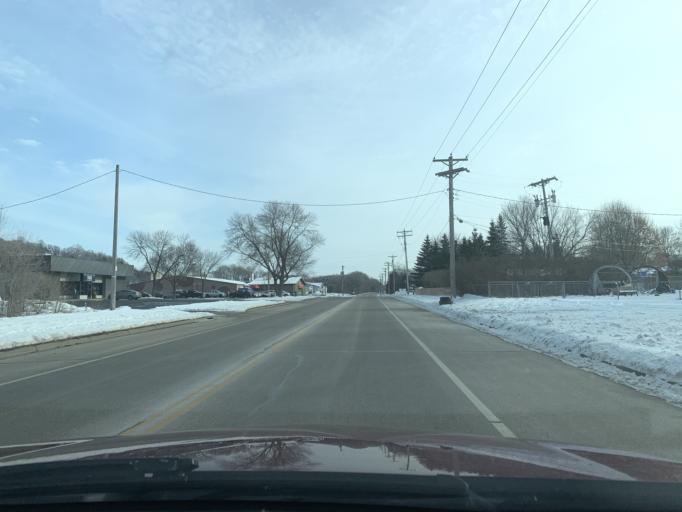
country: US
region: Minnesota
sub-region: Washington County
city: Saint Paul Park
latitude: 44.8401
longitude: -92.9781
